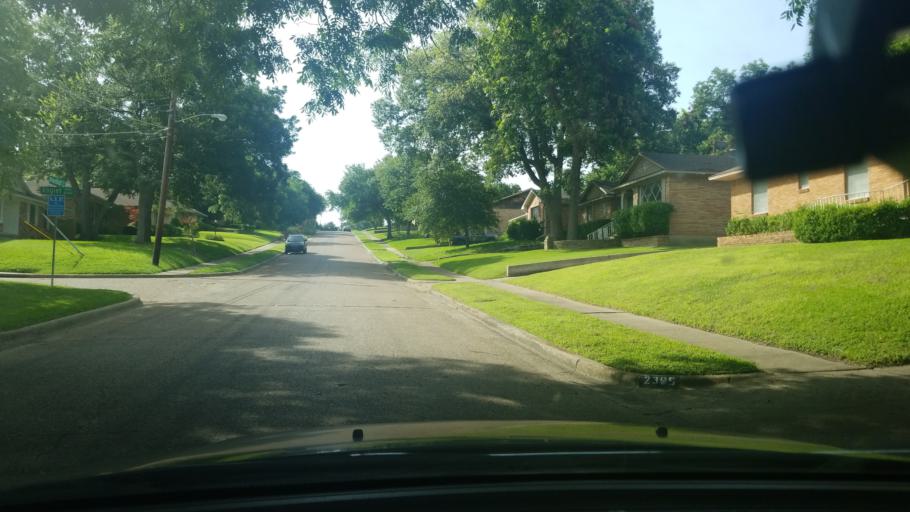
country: US
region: Texas
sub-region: Dallas County
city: Highland Park
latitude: 32.8068
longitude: -96.7073
